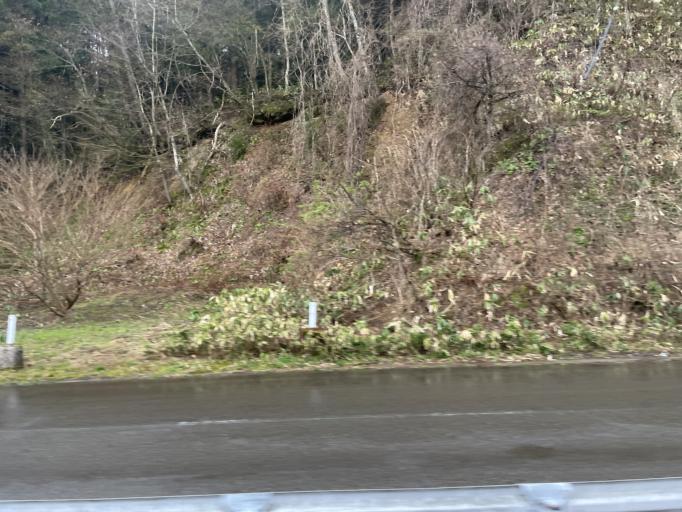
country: JP
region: Akita
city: Kakunodatemachi
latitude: 39.6828
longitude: 140.5539
